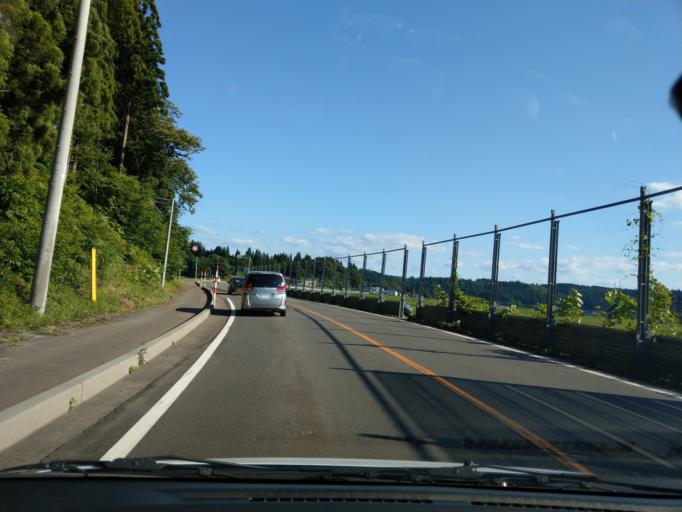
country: JP
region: Akita
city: Takanosu
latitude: 40.1835
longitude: 140.4004
